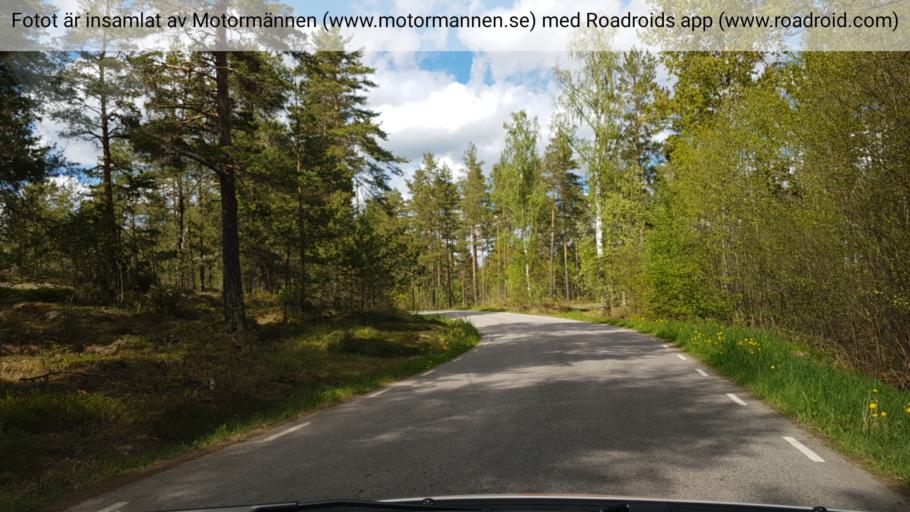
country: SE
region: Kalmar
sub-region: Vasterviks Kommun
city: Gamleby
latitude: 57.8878
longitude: 16.4386
